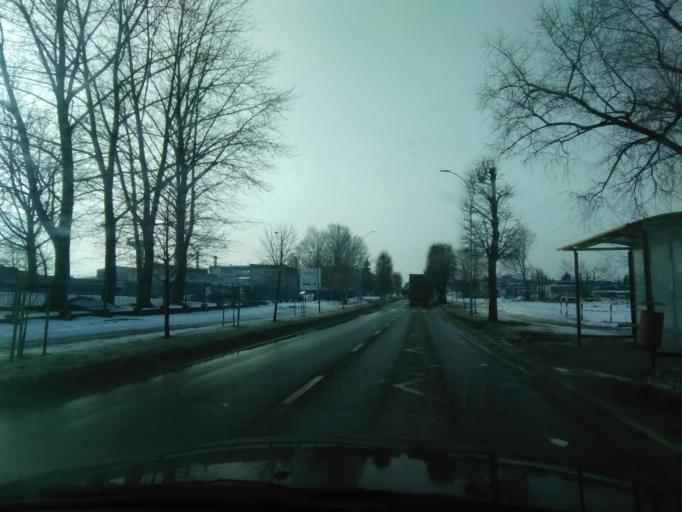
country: PL
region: Subcarpathian Voivodeship
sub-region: Krosno
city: Krosno
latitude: 49.7020
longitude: 21.7370
